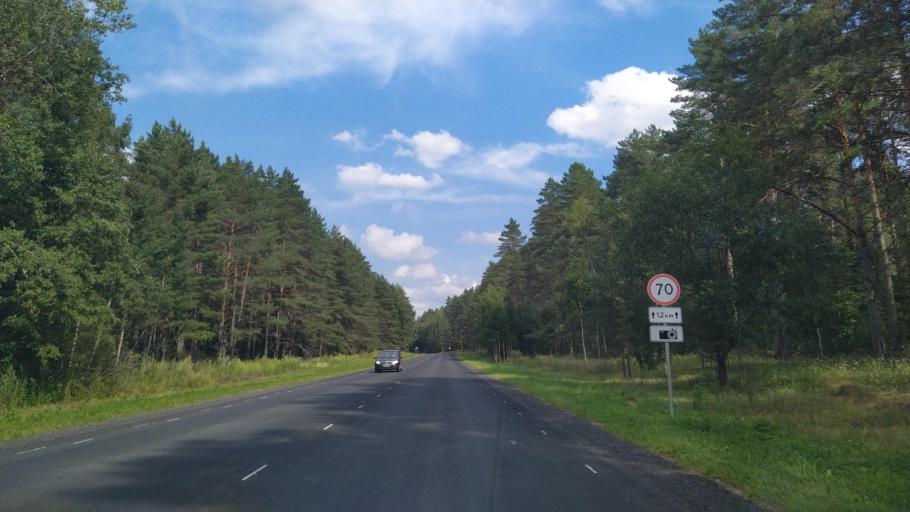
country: RU
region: Pskov
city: Porkhov
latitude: 57.7329
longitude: 29.3972
